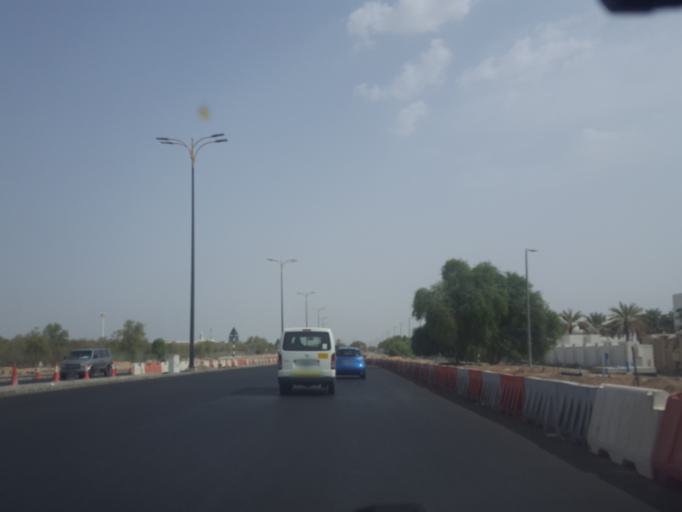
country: AE
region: Abu Dhabi
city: Al Ain
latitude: 24.2054
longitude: 55.7822
